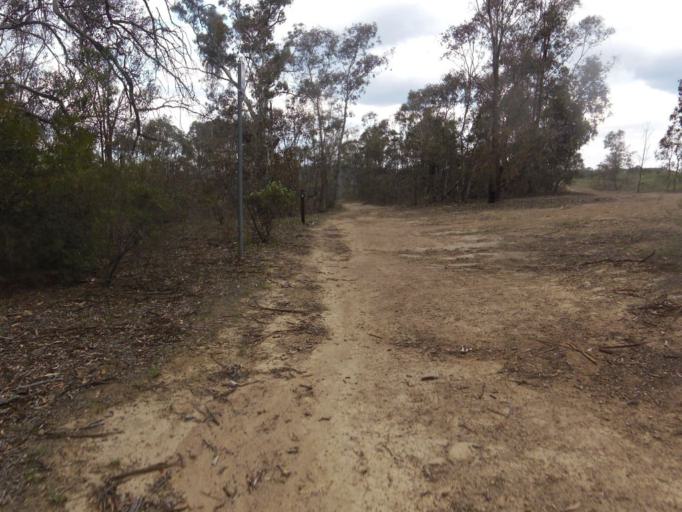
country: AU
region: Australian Capital Territory
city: Forrest
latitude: -35.3560
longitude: 149.1139
